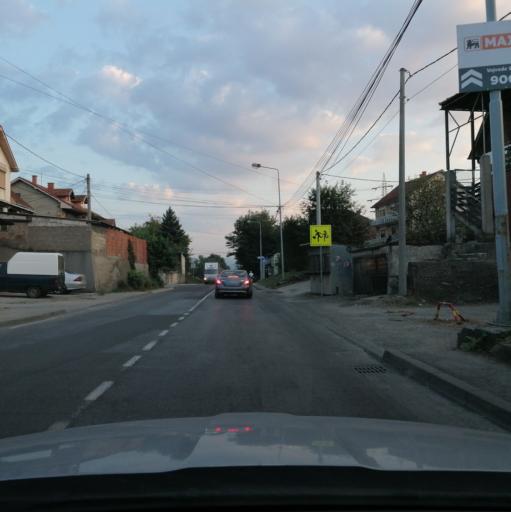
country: RS
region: Central Serbia
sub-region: Raski Okrug
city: Kraljevo
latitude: 43.7343
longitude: 20.6804
